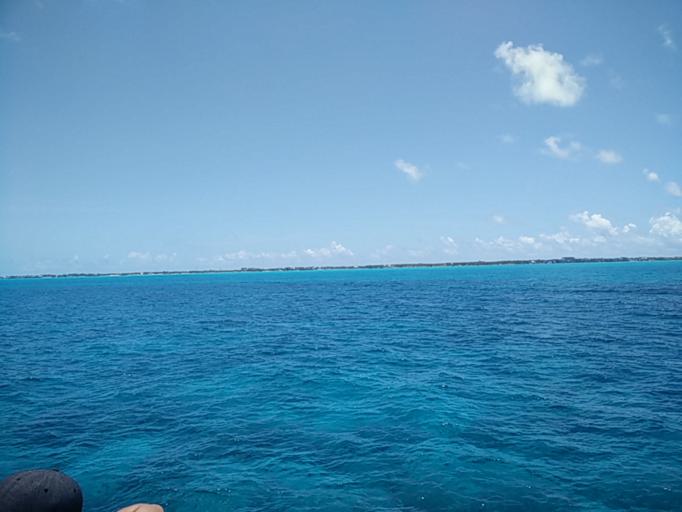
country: MX
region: Quintana Roo
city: Isla Mujeres
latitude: 21.2057
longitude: -86.7594
